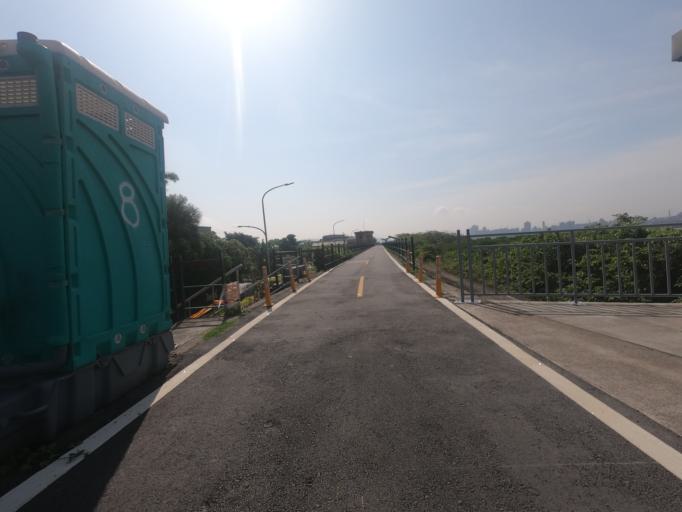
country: TW
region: Taipei
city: Taipei
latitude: 25.1076
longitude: 121.4694
